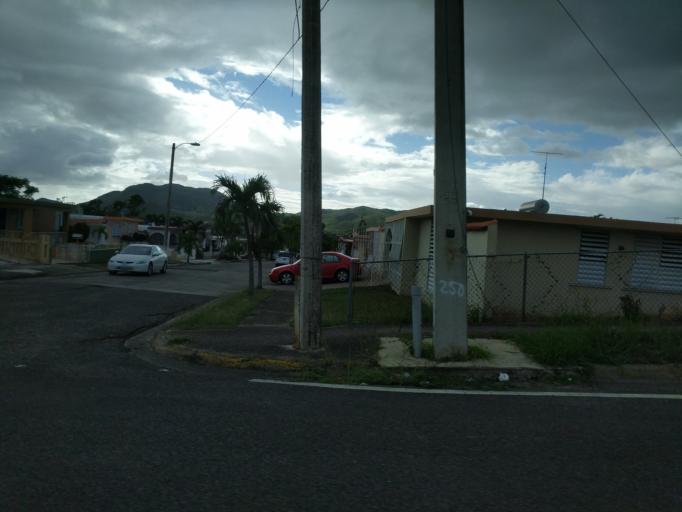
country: PR
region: Coamo
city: Coamo
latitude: 18.0784
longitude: -66.3683
